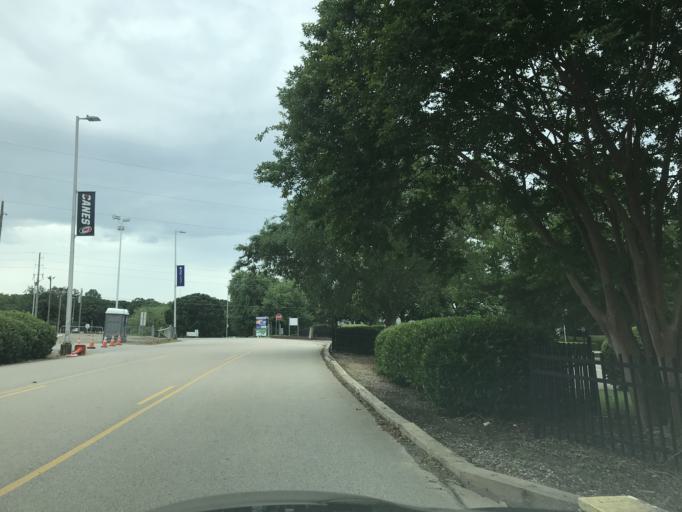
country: US
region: North Carolina
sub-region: Wake County
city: West Raleigh
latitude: 35.7996
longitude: -78.7170
